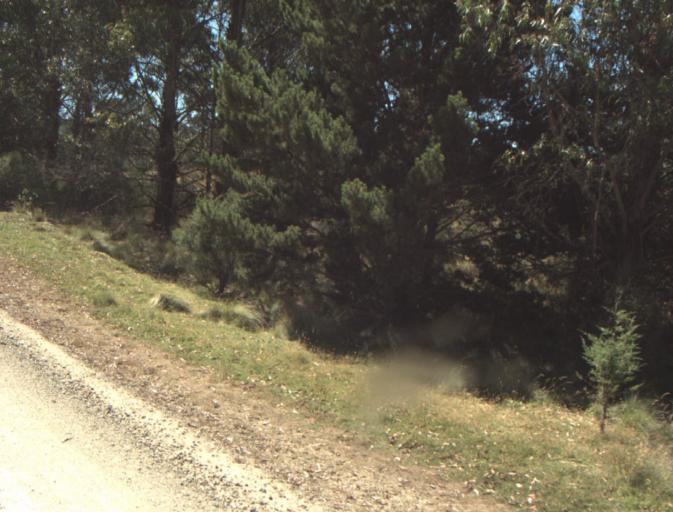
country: AU
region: Tasmania
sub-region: Dorset
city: Scottsdale
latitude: -41.3612
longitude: 147.4616
